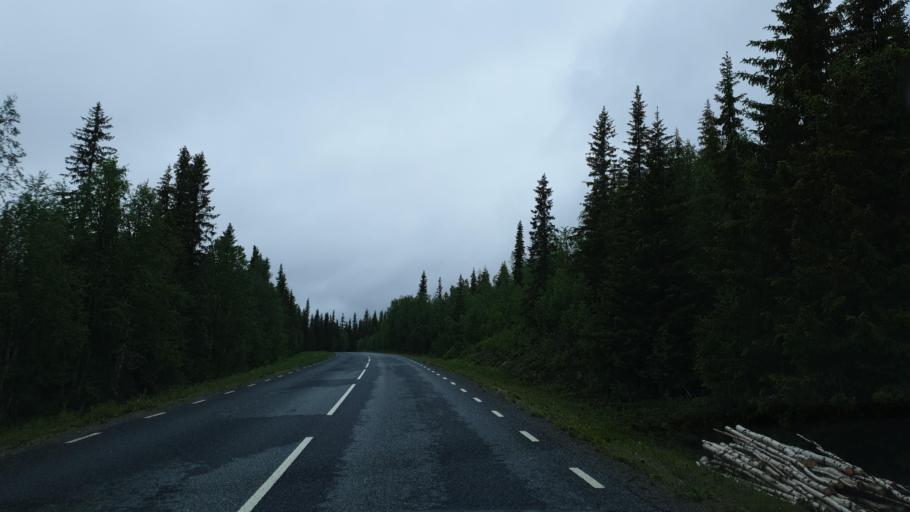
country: SE
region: Vaesterbotten
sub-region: Vilhelmina Kommun
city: Sjoberg
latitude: 65.2288
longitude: 15.8863
